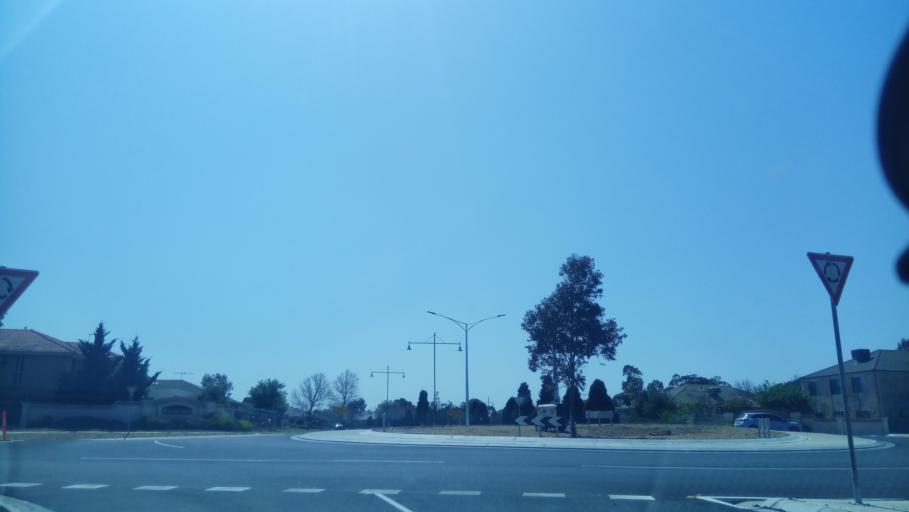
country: AU
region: Victoria
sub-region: Wyndham
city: Williams Landing
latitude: -37.8868
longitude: 144.7499
